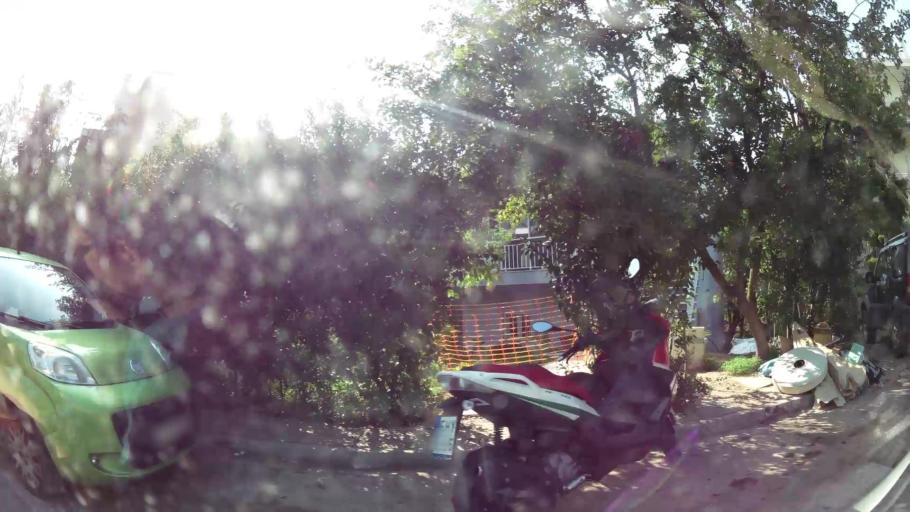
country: GR
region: Attica
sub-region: Nomarchia Athinas
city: Papagou
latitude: 37.9819
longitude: 23.7973
